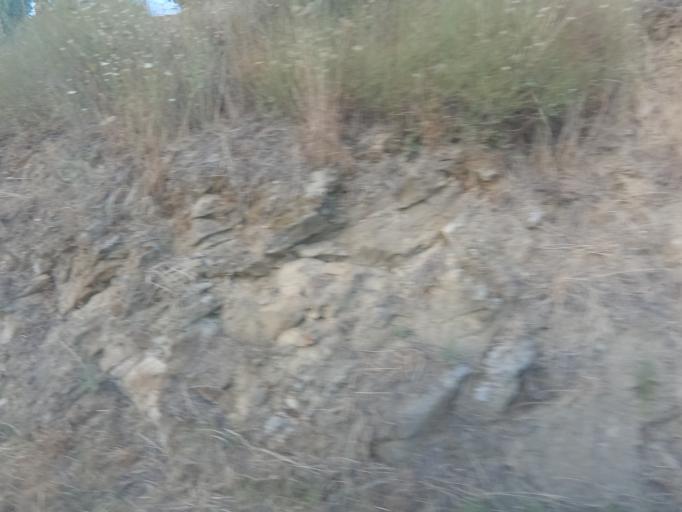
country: PT
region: Viseu
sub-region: Armamar
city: Armamar
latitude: 41.1678
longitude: -7.6854
